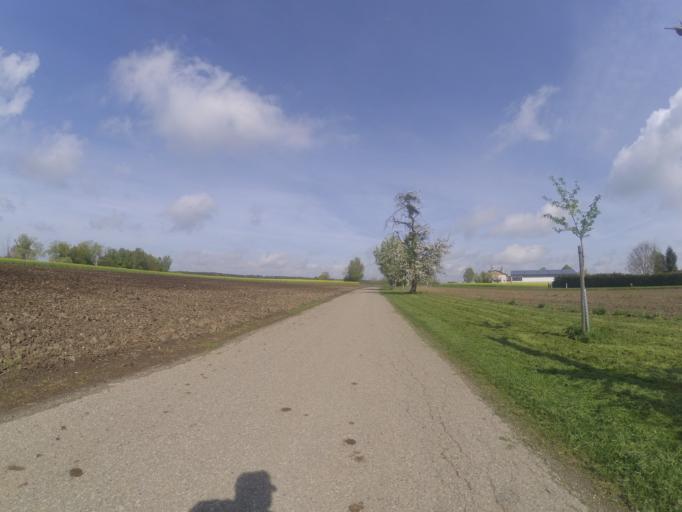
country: DE
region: Baden-Wuerttemberg
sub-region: Tuebingen Region
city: Griesingen
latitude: 48.2365
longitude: 9.8194
